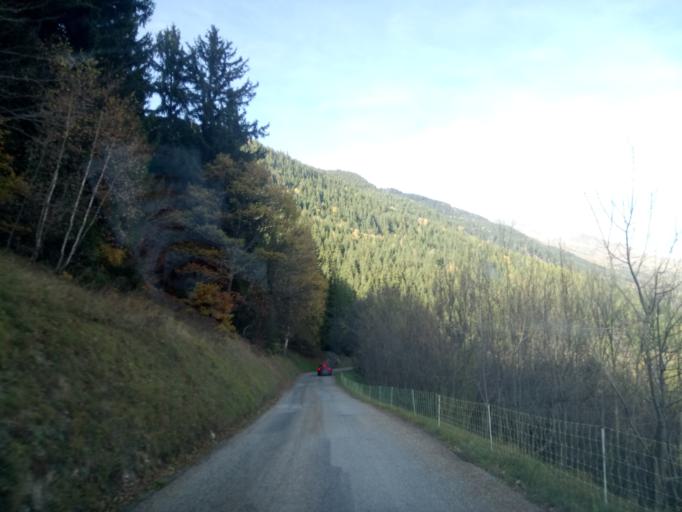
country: FR
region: Rhone-Alpes
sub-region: Departement de la Savoie
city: La Chambre
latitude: 45.3927
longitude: 6.3151
